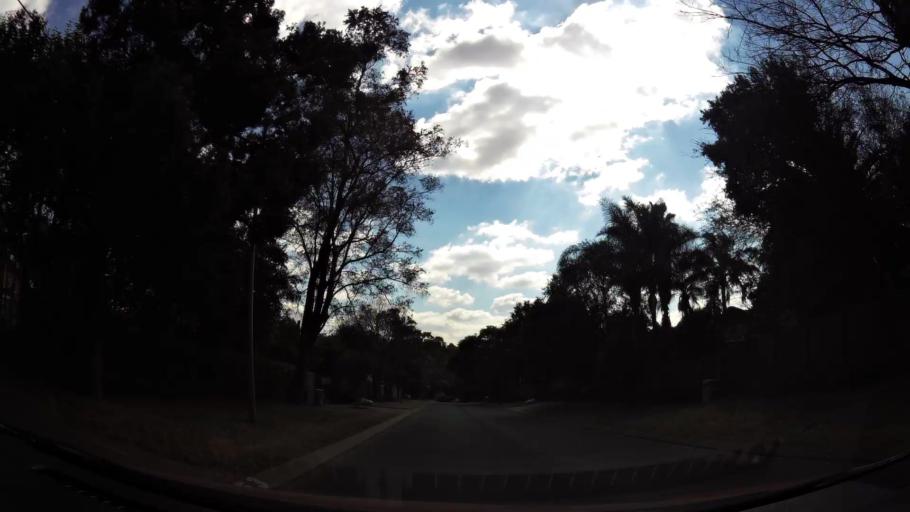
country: ZA
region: Gauteng
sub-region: City of Johannesburg Metropolitan Municipality
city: Roodepoort
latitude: -26.0760
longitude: 27.9495
